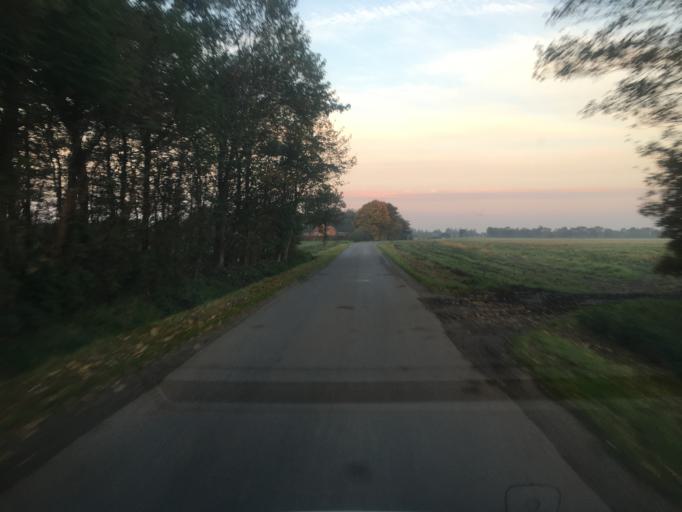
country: DK
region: South Denmark
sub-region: Tonder Kommune
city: Logumkloster
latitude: 54.9835
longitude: 9.0641
